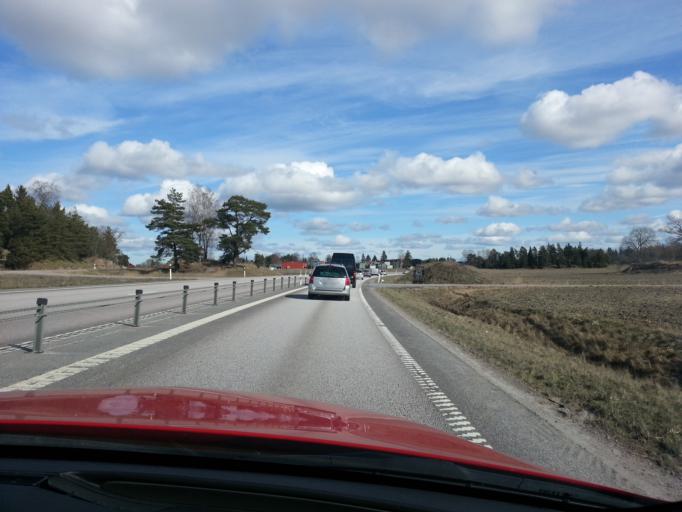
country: SE
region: Uppsala
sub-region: Uppsala Kommun
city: Vattholma
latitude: 59.9344
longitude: 17.8074
